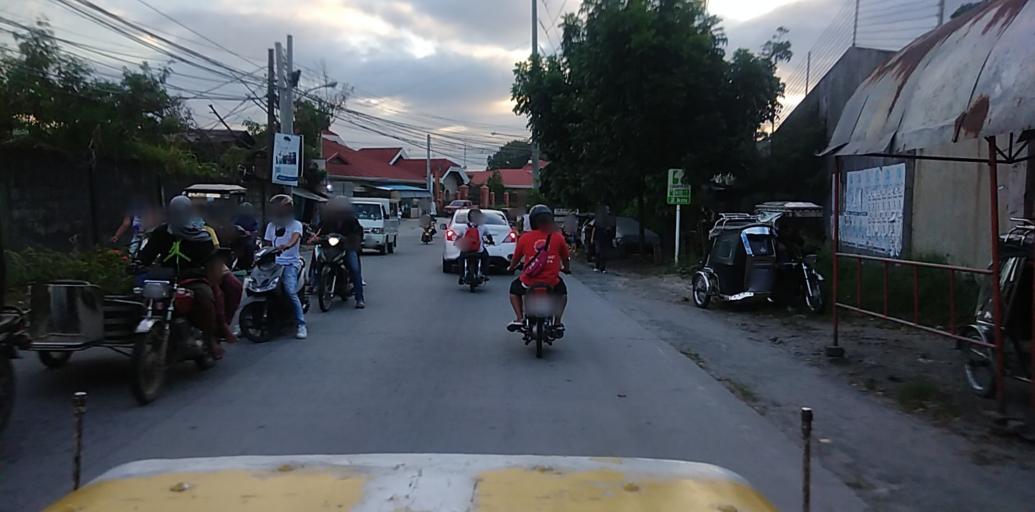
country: PH
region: Central Luzon
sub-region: Province of Pampanga
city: Telabastagan
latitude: 15.1181
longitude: 120.6037
